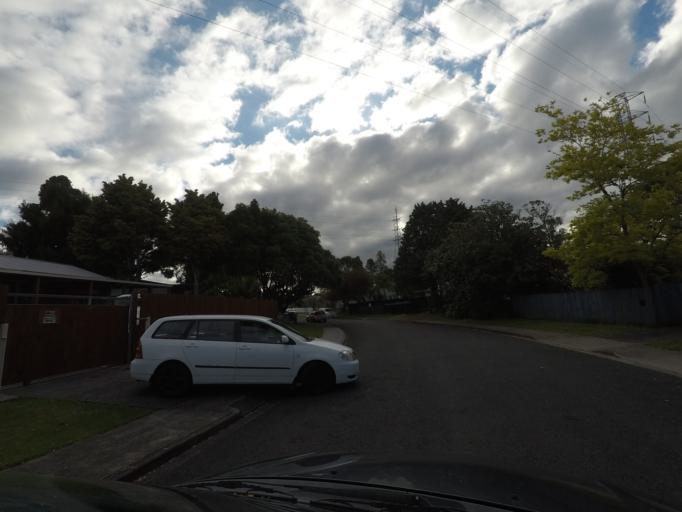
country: NZ
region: Auckland
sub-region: Auckland
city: Rosebank
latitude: -36.8818
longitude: 174.6587
